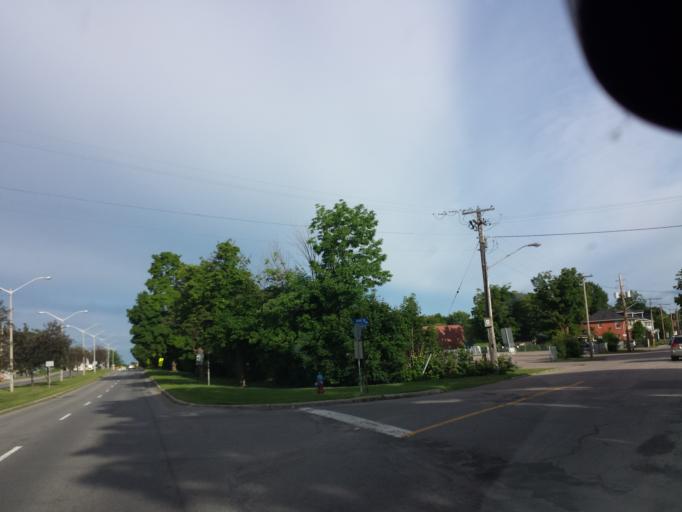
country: CA
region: Ontario
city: Renfrew
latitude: 45.4692
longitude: -76.6749
